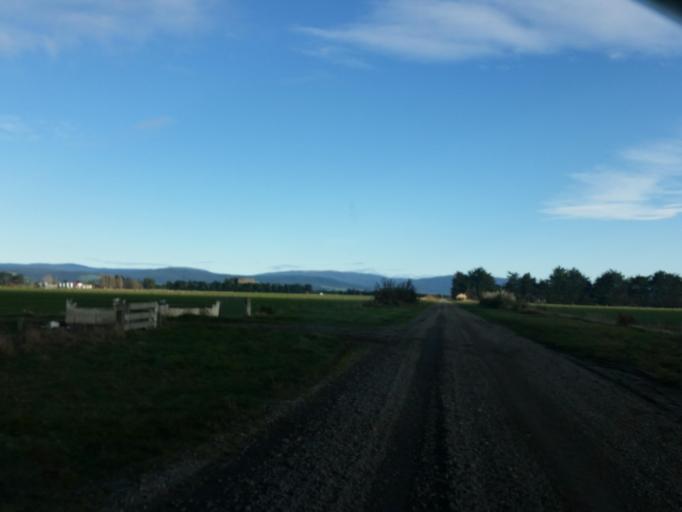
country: NZ
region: Southland
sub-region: Southland District
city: Winton
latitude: -46.1393
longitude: 168.1183
